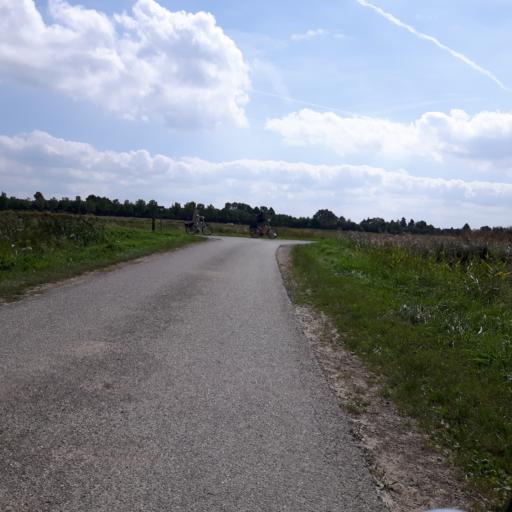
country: NL
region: Zeeland
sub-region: Gemeente Goes
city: Goes
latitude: 51.4659
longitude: 3.8973
